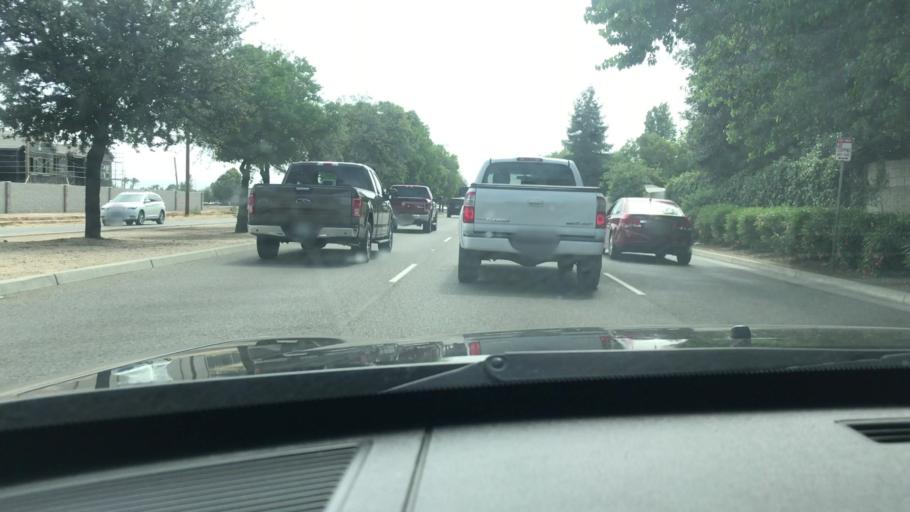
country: US
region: California
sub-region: Fresno County
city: Clovis
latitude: 36.8375
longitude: -119.7333
